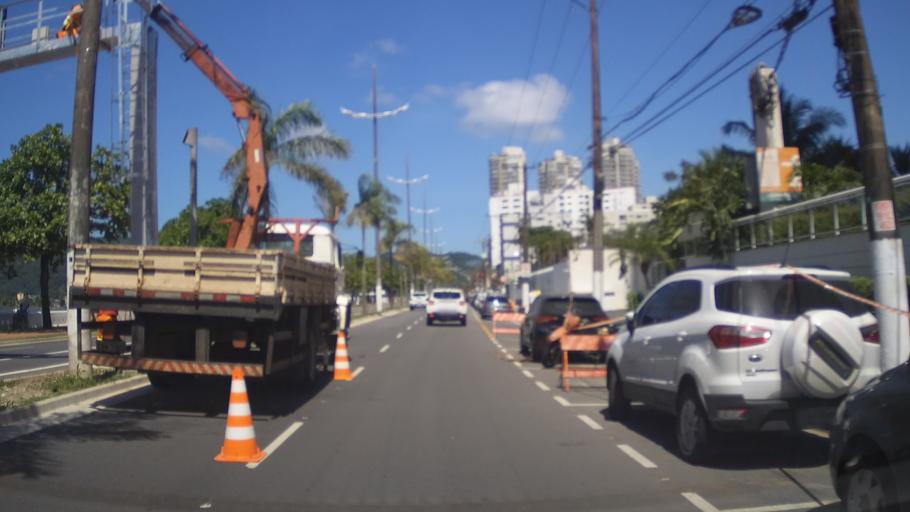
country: BR
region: Sao Paulo
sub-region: Guaruja
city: Guaruja
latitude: -23.9878
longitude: -46.2957
